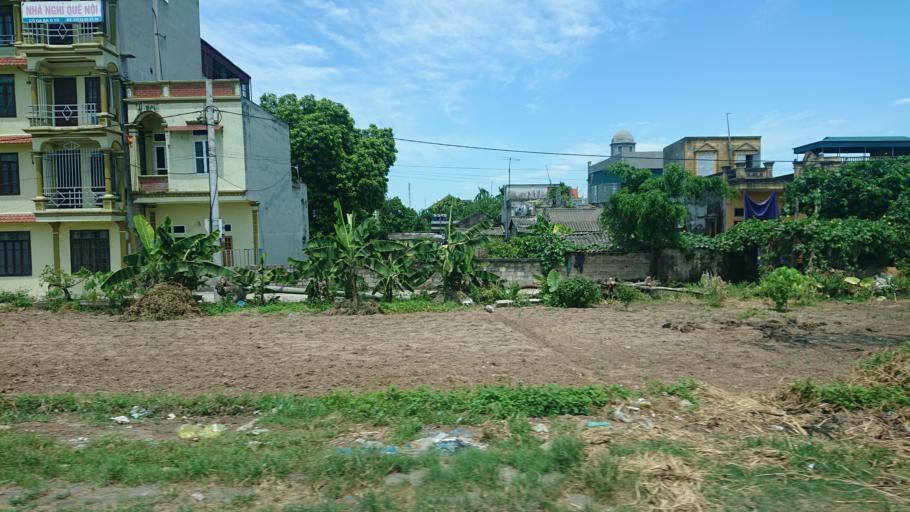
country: VN
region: Ha Nam
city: Thanh Pho Phu Ly
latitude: 20.5358
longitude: 105.9453
